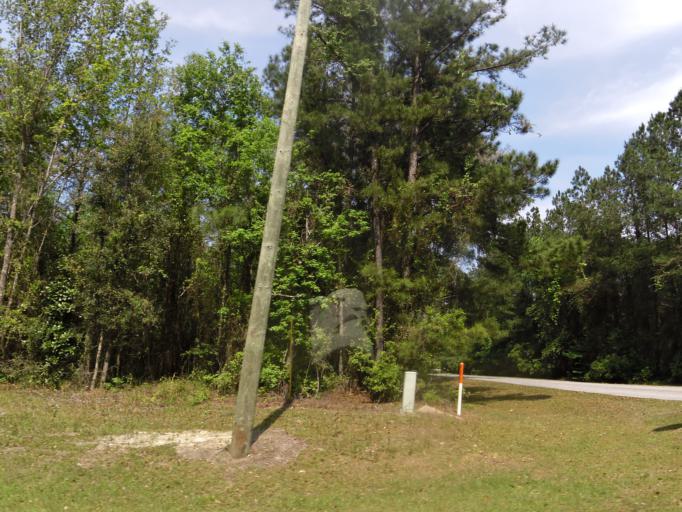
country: US
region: Georgia
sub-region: Camden County
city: Kingsland
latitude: 30.7989
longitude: -81.7219
